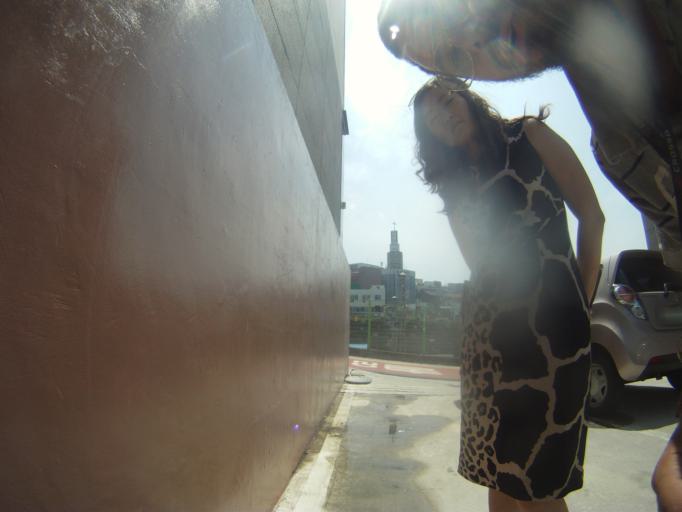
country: KR
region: Incheon
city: Incheon
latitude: 37.4745
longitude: 126.6184
